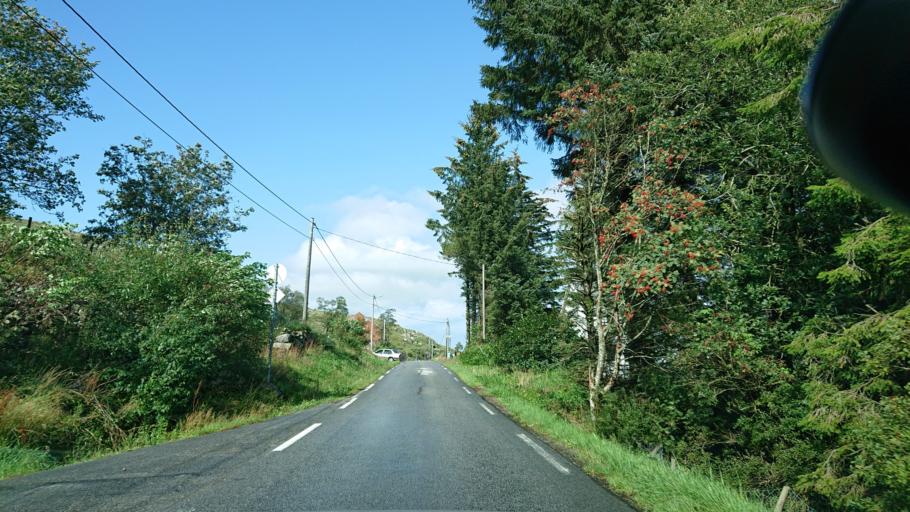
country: NO
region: Rogaland
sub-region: Gjesdal
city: Algard
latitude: 58.7005
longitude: 5.8904
